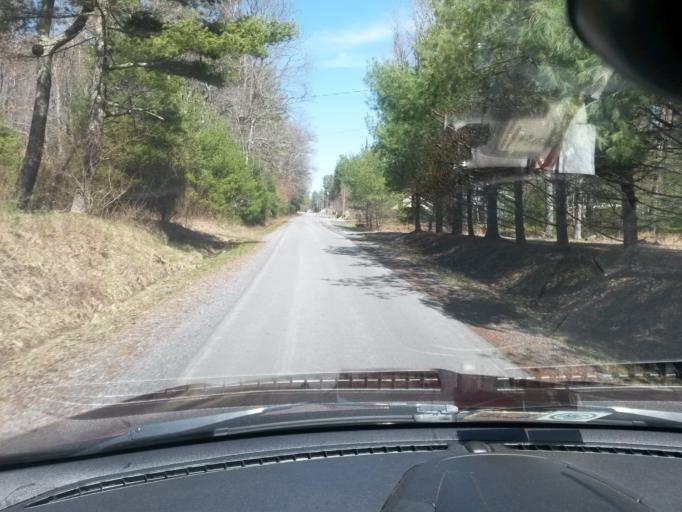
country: US
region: West Virginia
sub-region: Greenbrier County
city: Ronceverte
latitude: 37.6251
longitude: -80.3499
